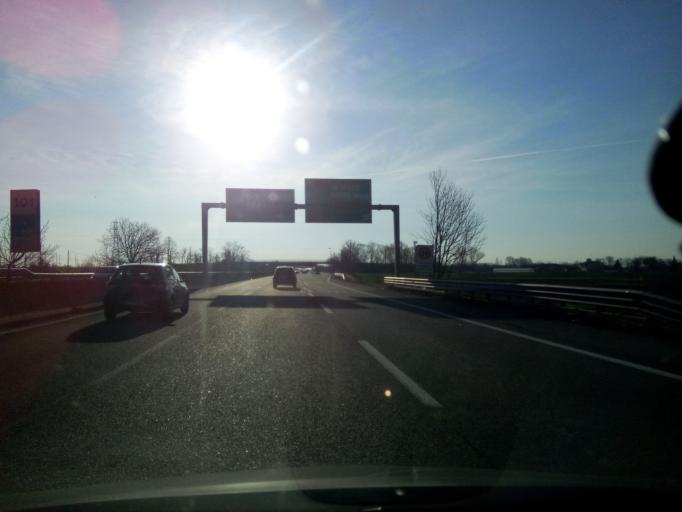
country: IT
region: Emilia-Romagna
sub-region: Provincia di Parma
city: Ponte Taro
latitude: 44.8675
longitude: 10.2230
